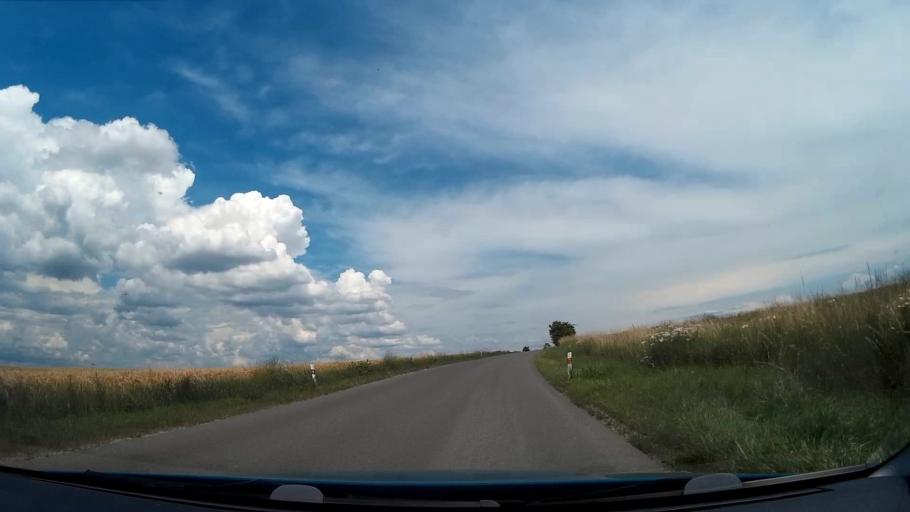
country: CZ
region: South Moravian
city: Orechov
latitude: 49.0696
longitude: 16.5277
